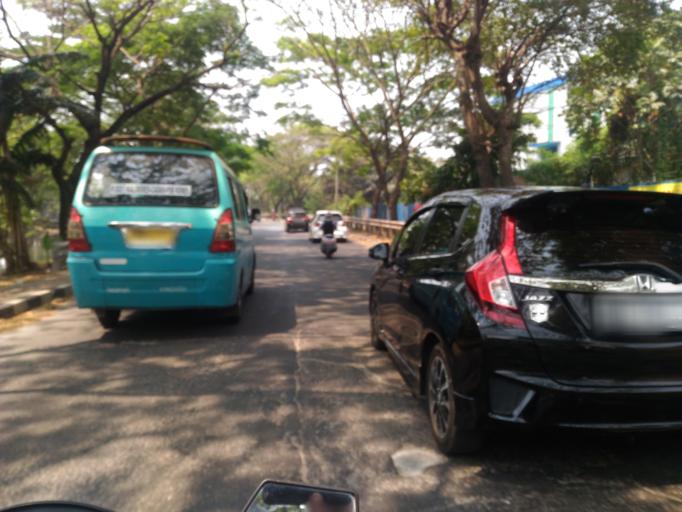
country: ID
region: Banten
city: Tangerang
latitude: -6.1604
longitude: 106.6140
